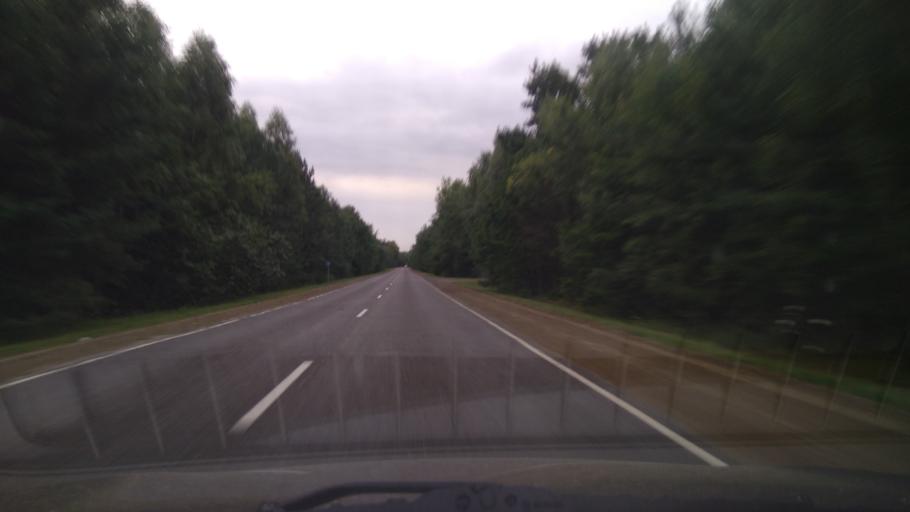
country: BY
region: Brest
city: Byaroza
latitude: 52.4081
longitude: 24.9965
